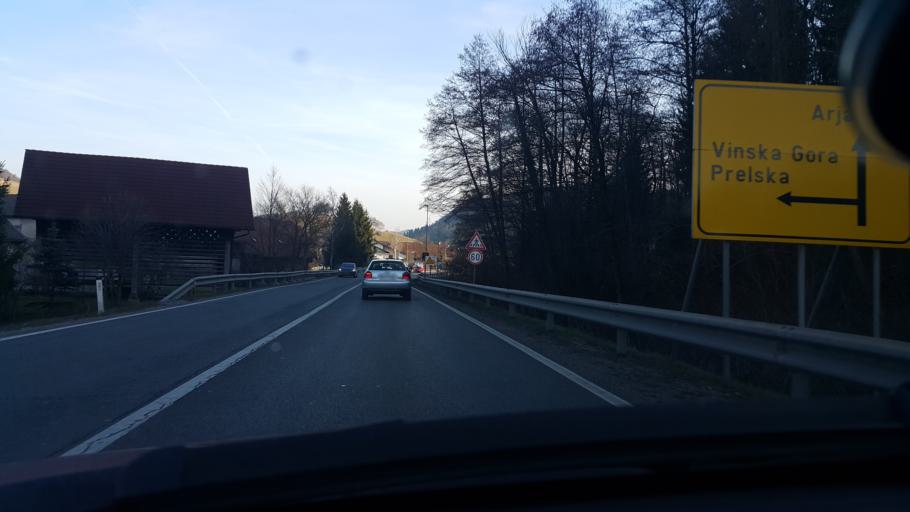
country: SI
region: Dobrna
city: Dobrna
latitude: 46.3423
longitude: 15.1701
